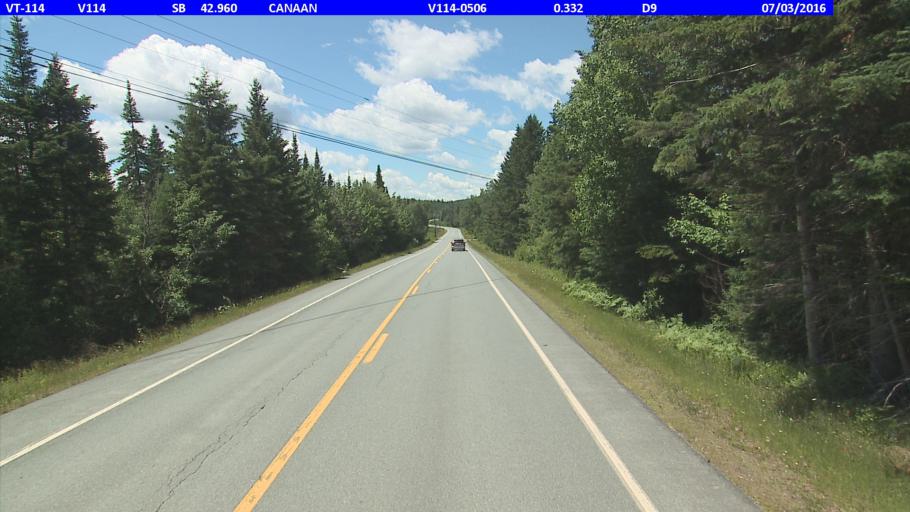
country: CA
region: Quebec
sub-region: Estrie
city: Coaticook
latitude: 45.0053
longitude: -71.6868
